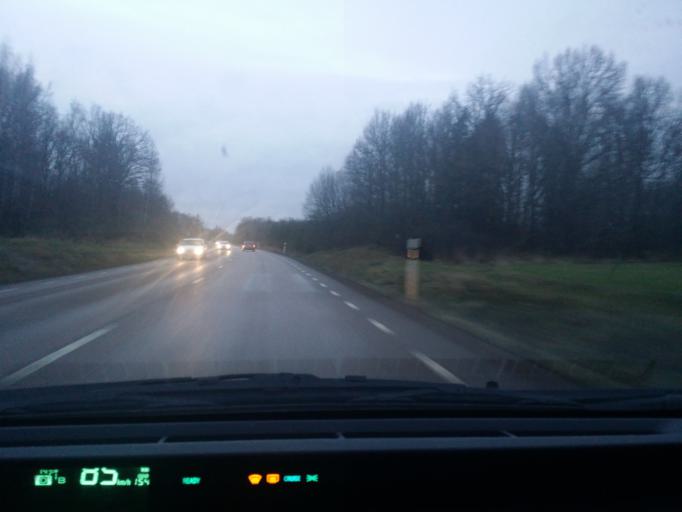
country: SE
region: Soedermanland
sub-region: Eskilstuna Kommun
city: Kvicksund
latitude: 59.4675
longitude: 16.3133
